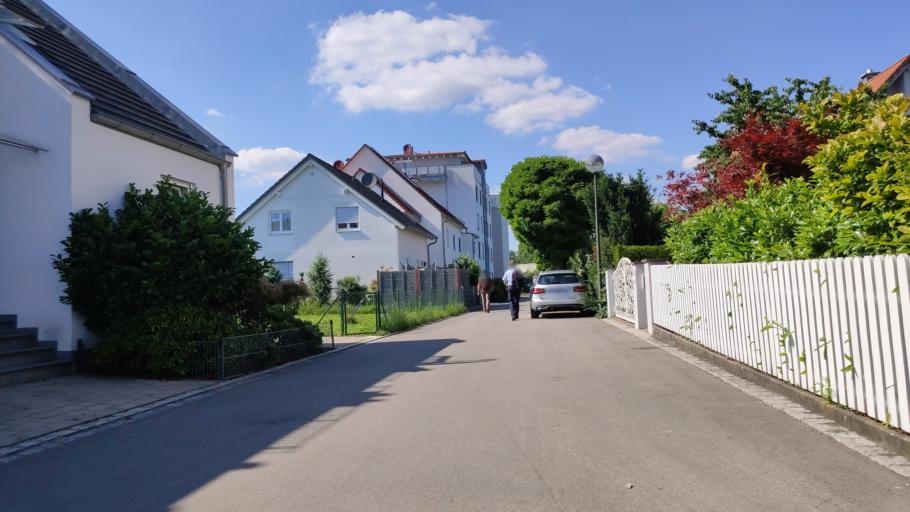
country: DE
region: Bavaria
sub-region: Swabia
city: Mering
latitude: 48.2640
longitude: 10.9835
